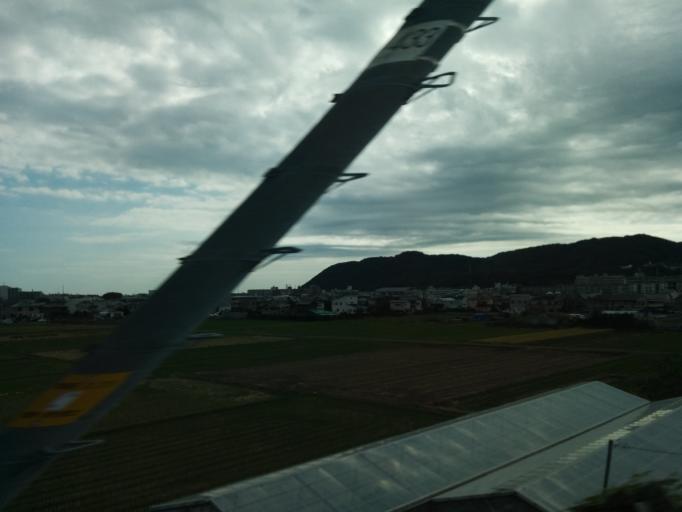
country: JP
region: Kanagawa
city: Oiso
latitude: 35.3404
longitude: 139.3058
